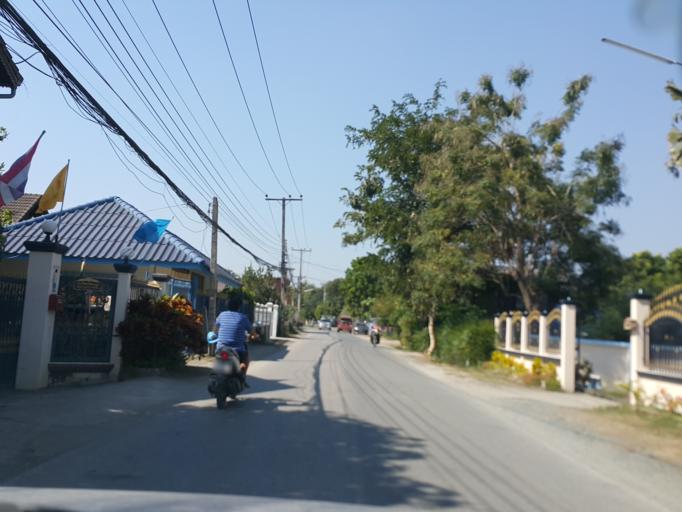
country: TH
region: Chiang Mai
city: San Kamphaeng
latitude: 18.7406
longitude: 99.1048
